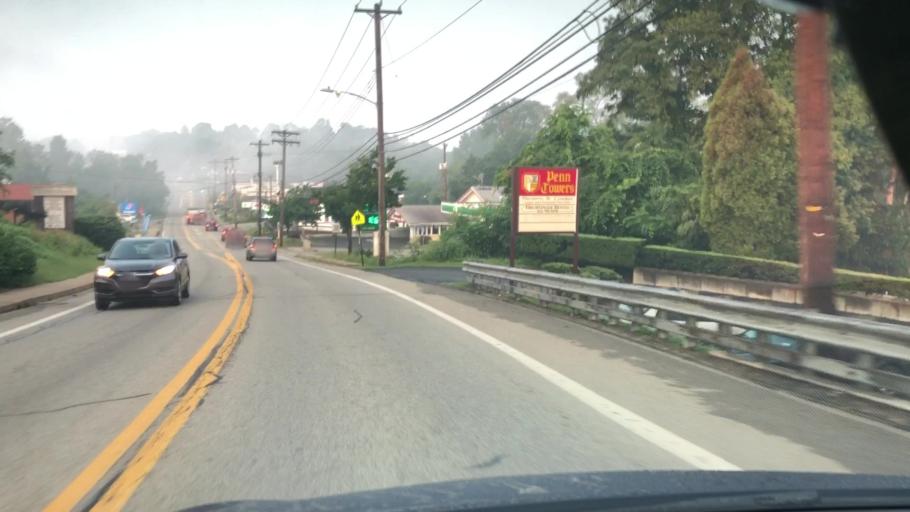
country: US
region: Pennsylvania
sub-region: Allegheny County
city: Monroeville
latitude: 40.4267
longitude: -79.7756
